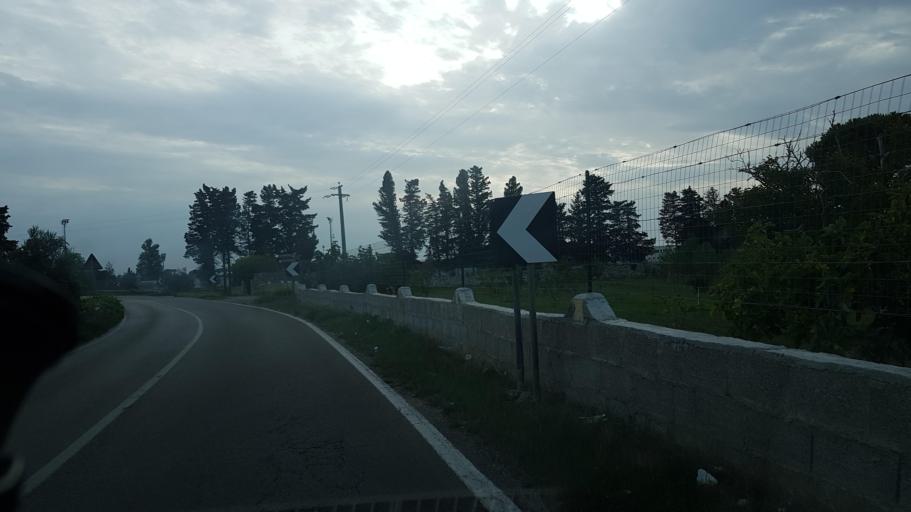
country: IT
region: Apulia
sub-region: Provincia di Lecce
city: Trepuzzi
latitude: 40.4273
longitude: 18.0732
